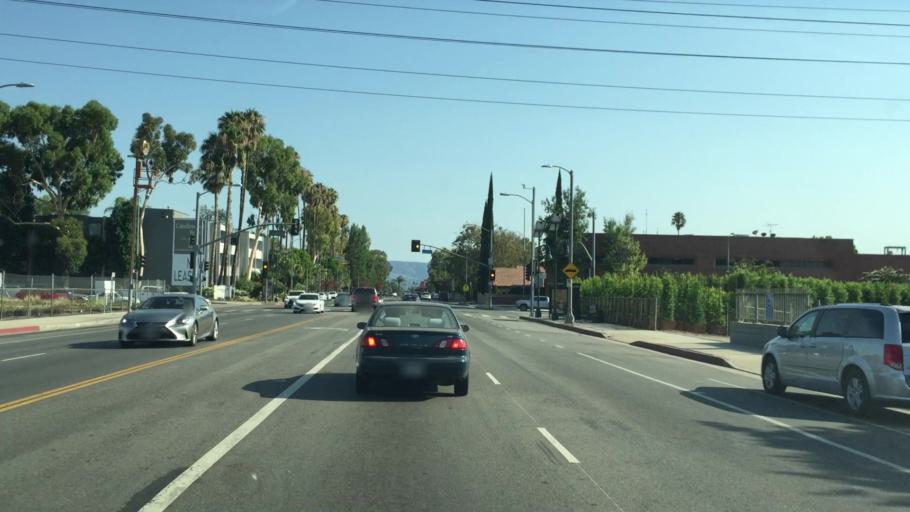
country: US
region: California
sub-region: Los Angeles County
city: Northridge
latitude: 34.2508
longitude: -118.5361
